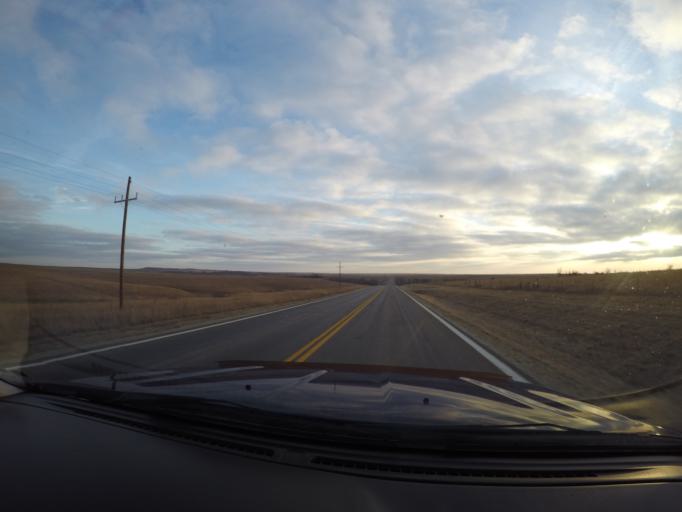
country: US
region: Kansas
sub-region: Morris County
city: Council Grove
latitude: 38.6244
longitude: -96.4947
